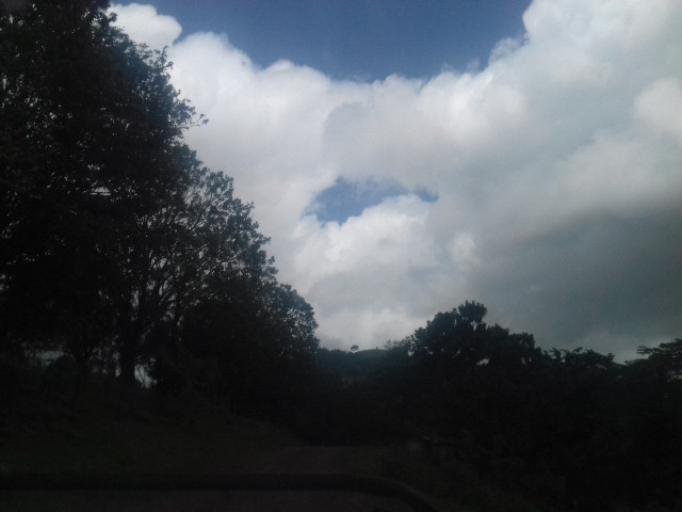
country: NI
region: Matagalpa
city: Matiguas
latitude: 12.9097
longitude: -85.3606
